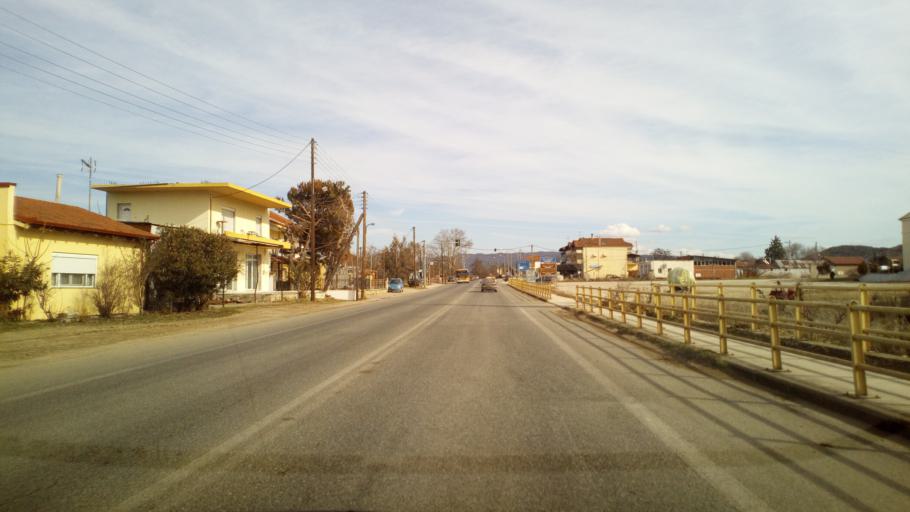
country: GR
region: Central Macedonia
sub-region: Nomos Thessalonikis
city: Gerakarou
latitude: 40.6309
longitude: 23.2132
